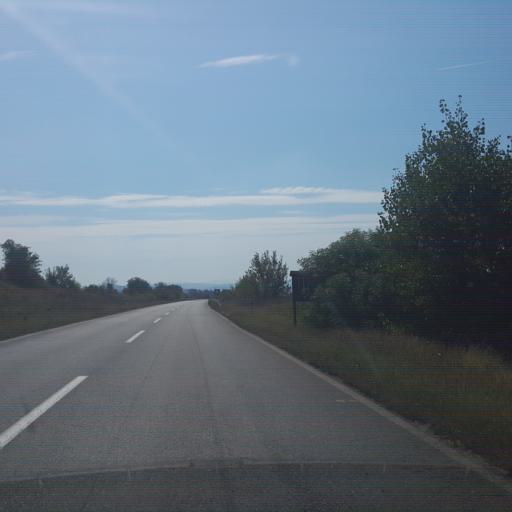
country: RS
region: Central Serbia
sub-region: Zajecarski Okrug
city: Knjazevac
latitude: 43.6370
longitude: 22.2821
